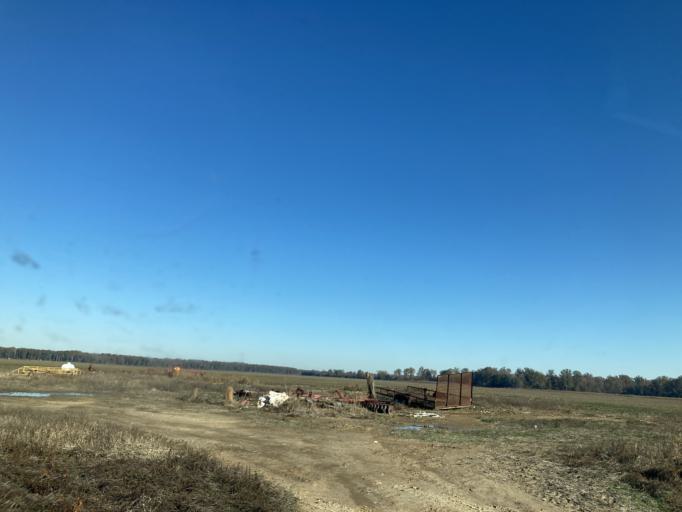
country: US
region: Mississippi
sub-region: Sharkey County
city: Rolling Fork
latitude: 32.9012
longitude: -90.6598
